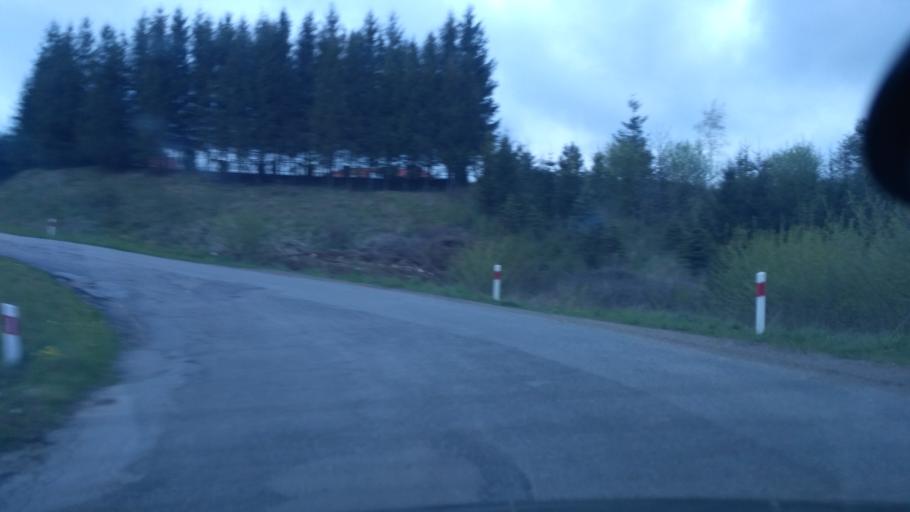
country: PL
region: Subcarpathian Voivodeship
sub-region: Powiat sanocki
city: Sanok
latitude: 49.6283
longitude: 22.2776
